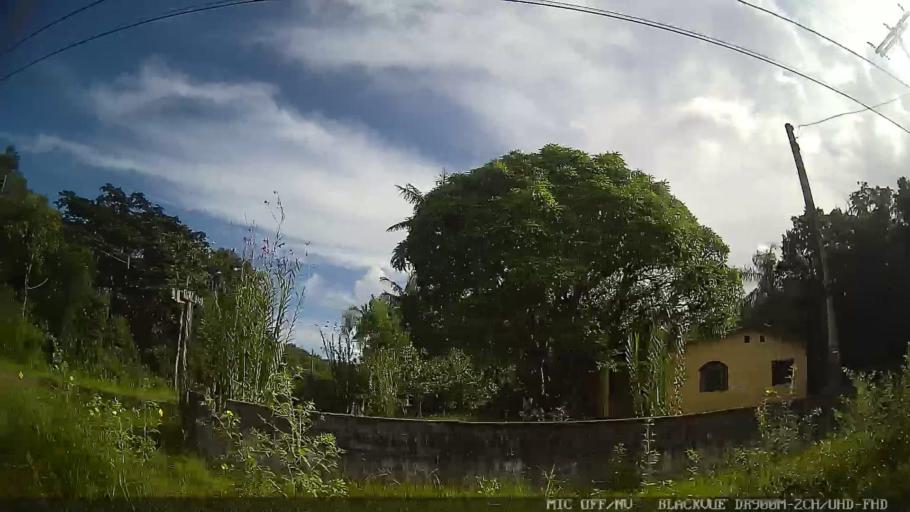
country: BR
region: Sao Paulo
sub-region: Itanhaem
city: Itanhaem
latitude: -24.2048
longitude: -46.8853
